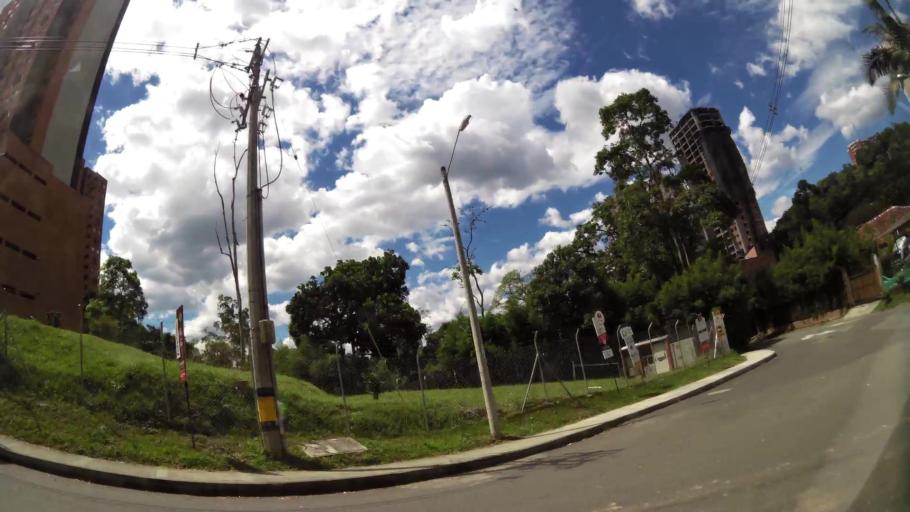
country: CO
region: Antioquia
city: Sabaneta
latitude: 6.1443
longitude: -75.6167
